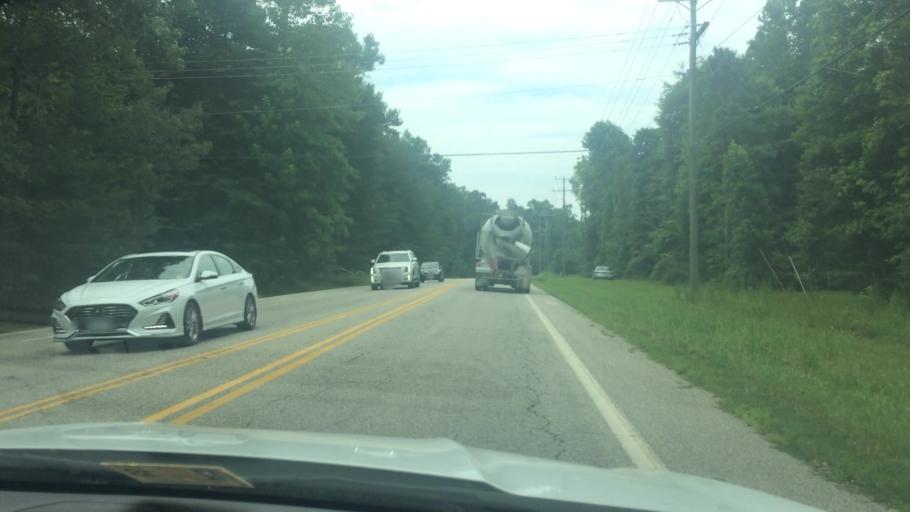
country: US
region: Virginia
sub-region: James City County
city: Williamsburg
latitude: 37.2925
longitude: -76.7992
